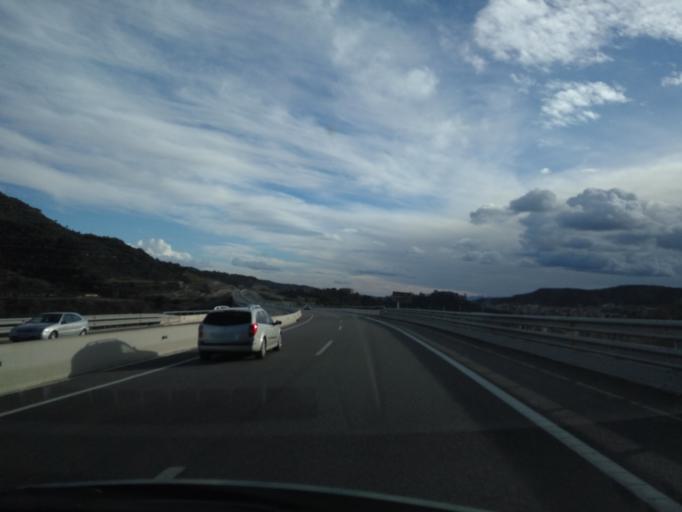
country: ES
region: Catalonia
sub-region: Provincia de Barcelona
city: Puig-reig
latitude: 41.9870
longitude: 1.8837
